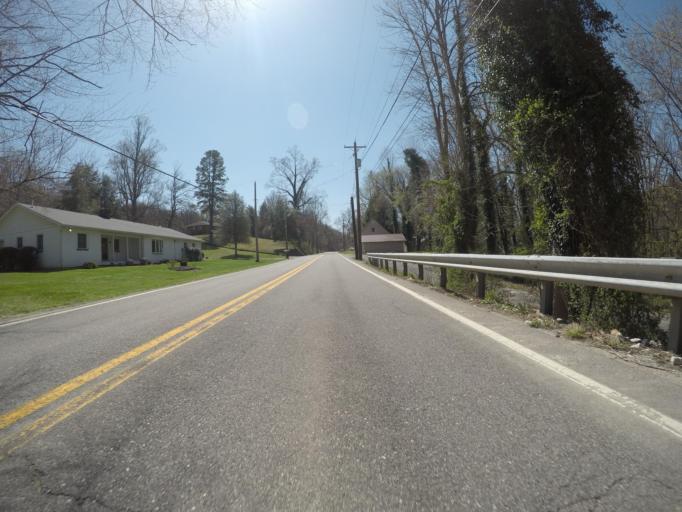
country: US
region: West Virginia
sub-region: Kanawha County
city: Pinch
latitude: 38.4005
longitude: -81.5475
